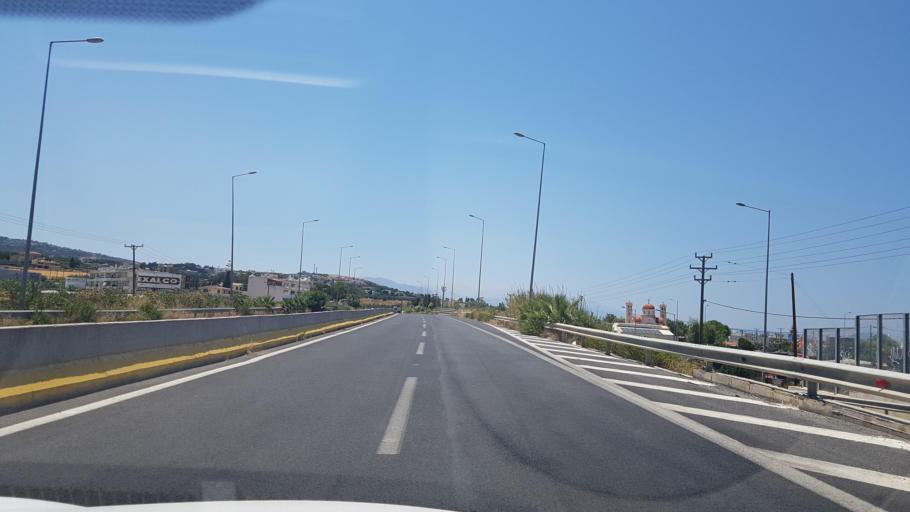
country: GR
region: Crete
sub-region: Nomos Rethymnis
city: Rethymno
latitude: 35.3655
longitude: 24.5170
